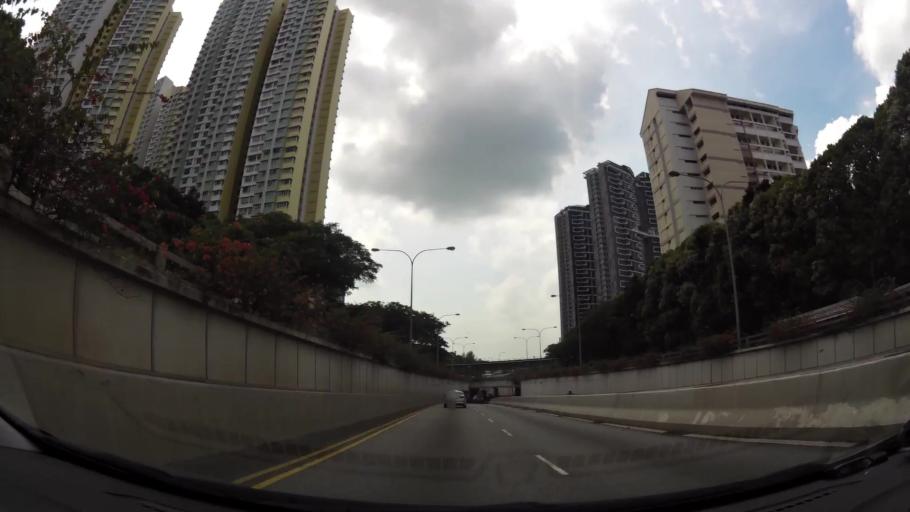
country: SG
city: Singapore
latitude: 1.3205
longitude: 103.7638
